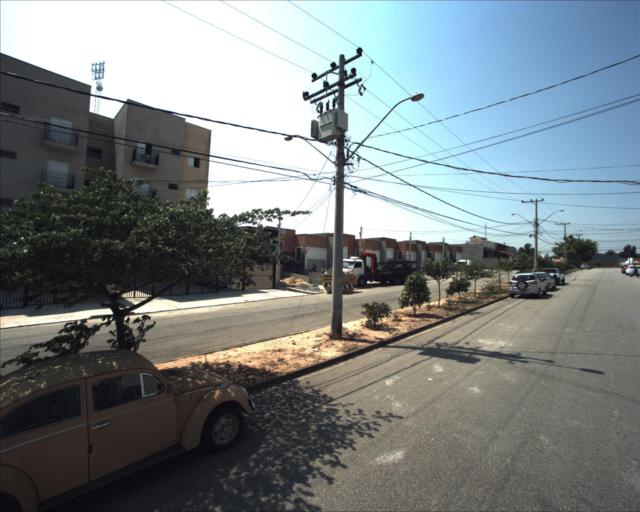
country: BR
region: Sao Paulo
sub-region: Sorocaba
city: Sorocaba
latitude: -23.4350
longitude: -47.4857
